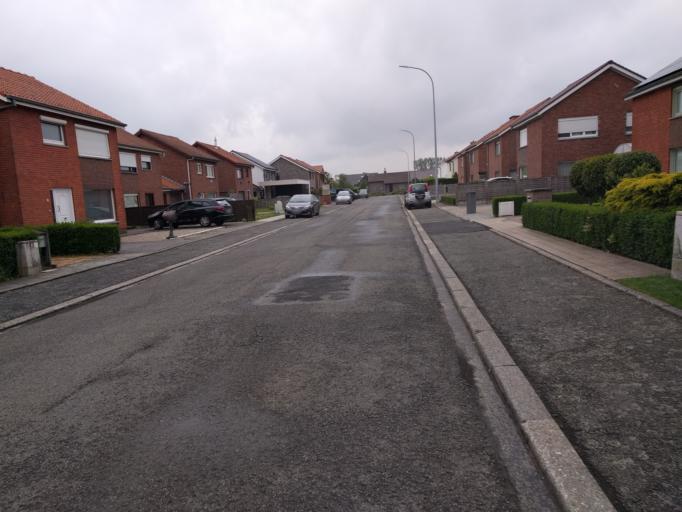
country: BE
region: Flanders
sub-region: Provincie West-Vlaanderen
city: Wevelgem
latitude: 50.8345
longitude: 3.2051
